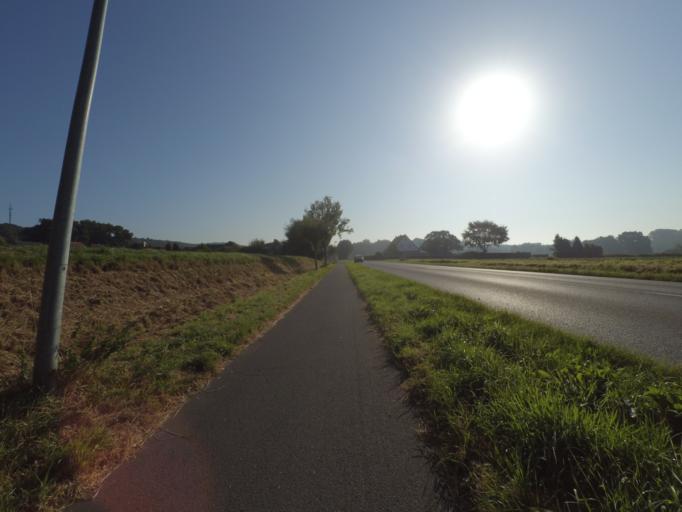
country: DE
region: Lower Saxony
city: Bad Bentheim
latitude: 52.2980
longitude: 7.1721
